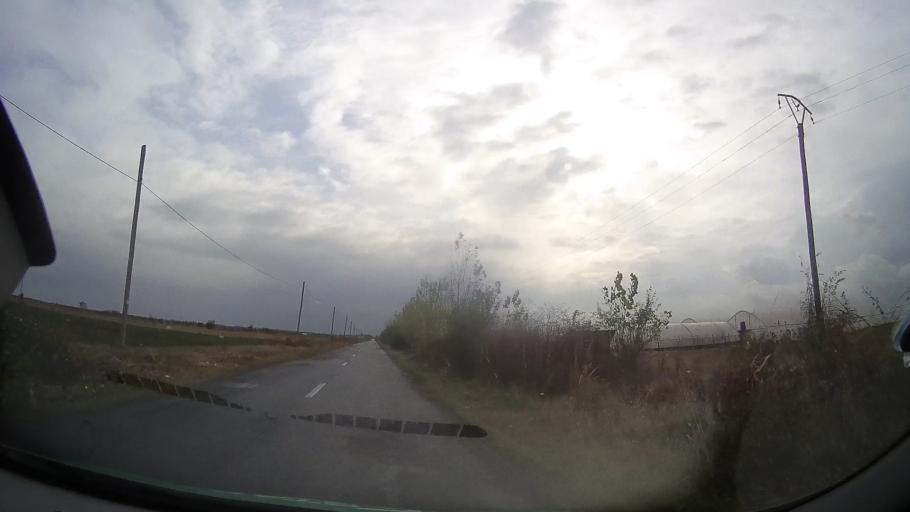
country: RO
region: Ialomita
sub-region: Comuna Fierbinti-Targ
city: Fierbintii de Jos
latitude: 44.7129
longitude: 26.3908
